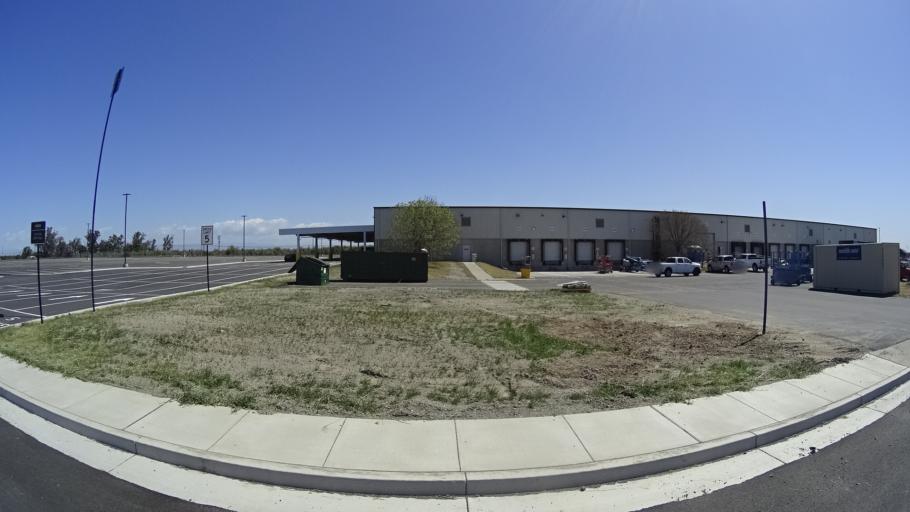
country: US
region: California
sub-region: Glenn County
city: Orland
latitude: 39.7193
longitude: -122.1433
